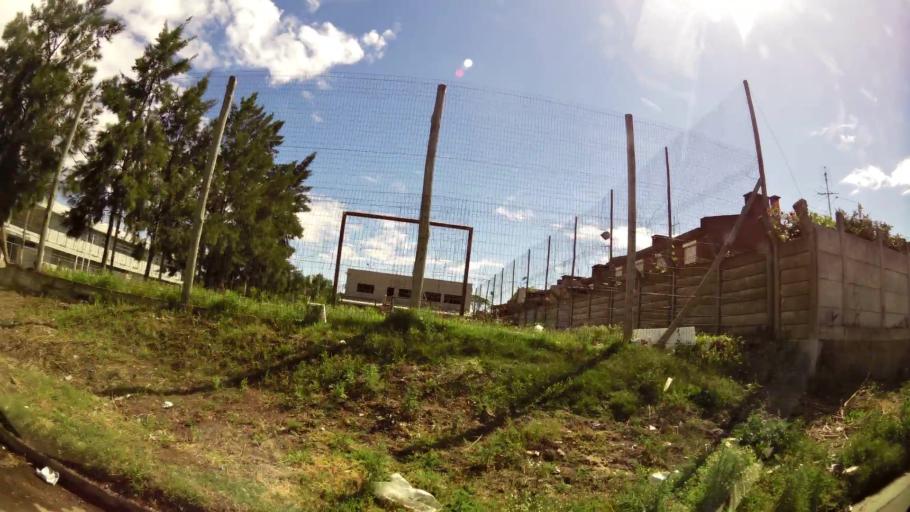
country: UY
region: Montevideo
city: Montevideo
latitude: -34.8454
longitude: -56.1895
